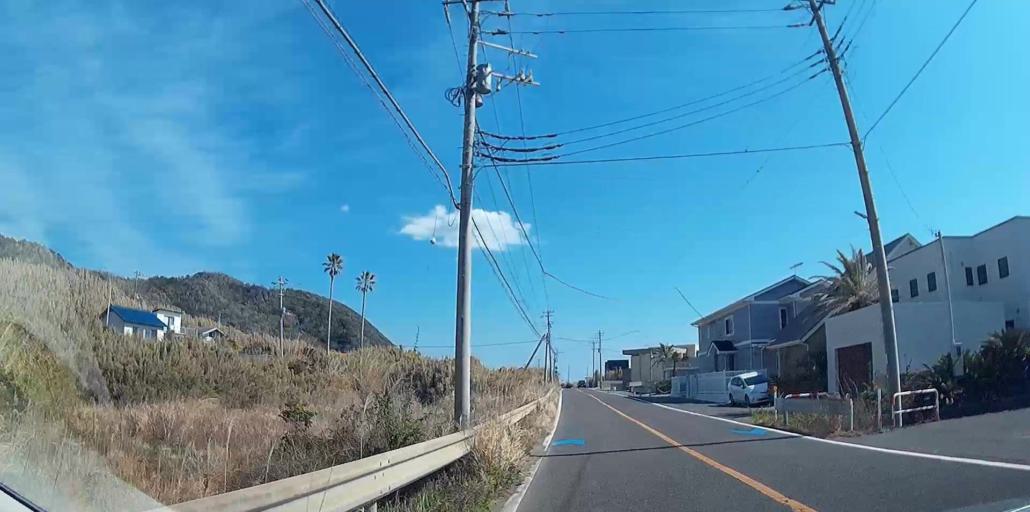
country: JP
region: Chiba
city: Tateyama
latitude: 34.9598
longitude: 139.7632
